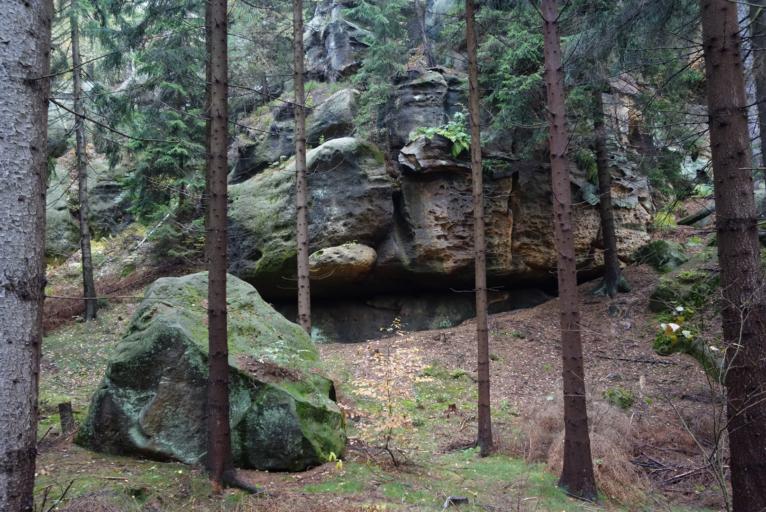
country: DE
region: Saxony
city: Kurort Oybin
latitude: 50.8379
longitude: 14.7275
